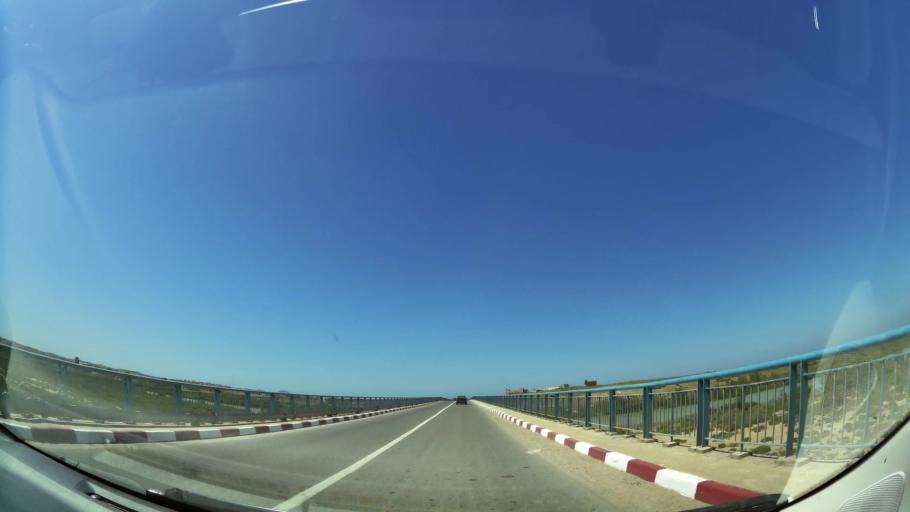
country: MA
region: Oriental
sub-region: Berkane-Taourirt
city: Madagh
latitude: 35.1080
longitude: -2.3612
